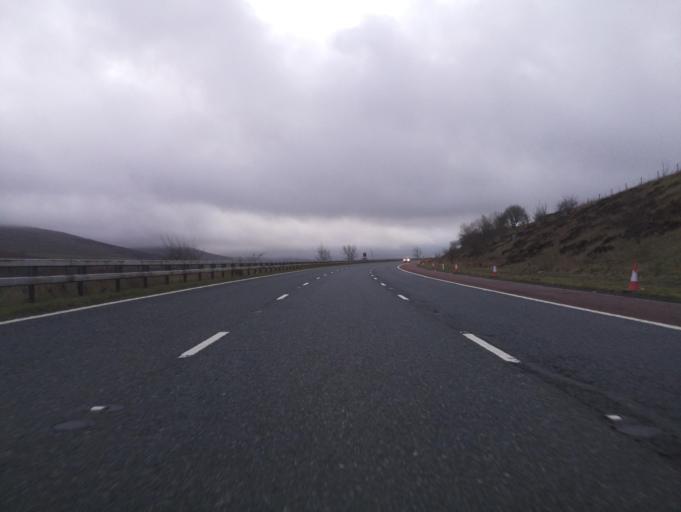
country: GB
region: England
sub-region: Cumbria
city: Sedbergh
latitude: 54.3833
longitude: -2.5826
